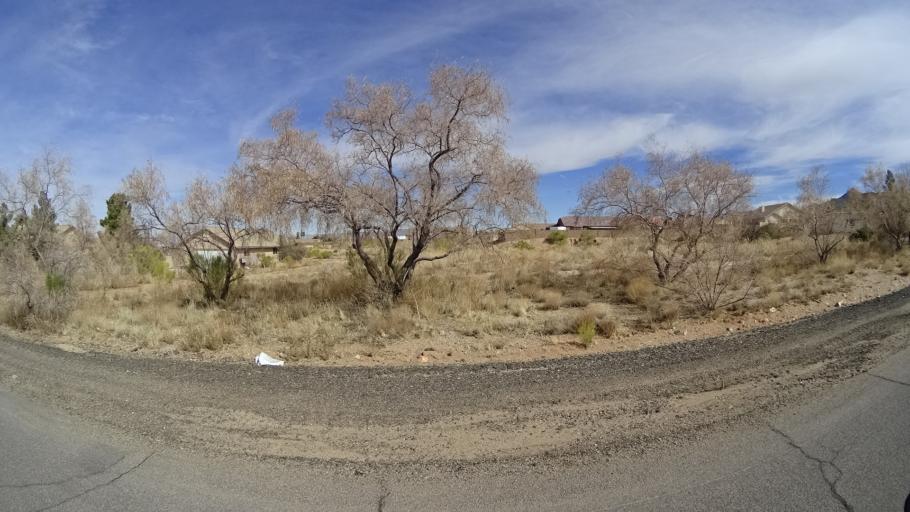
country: US
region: Arizona
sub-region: Mohave County
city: Kingman
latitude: 35.1913
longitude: -113.9833
